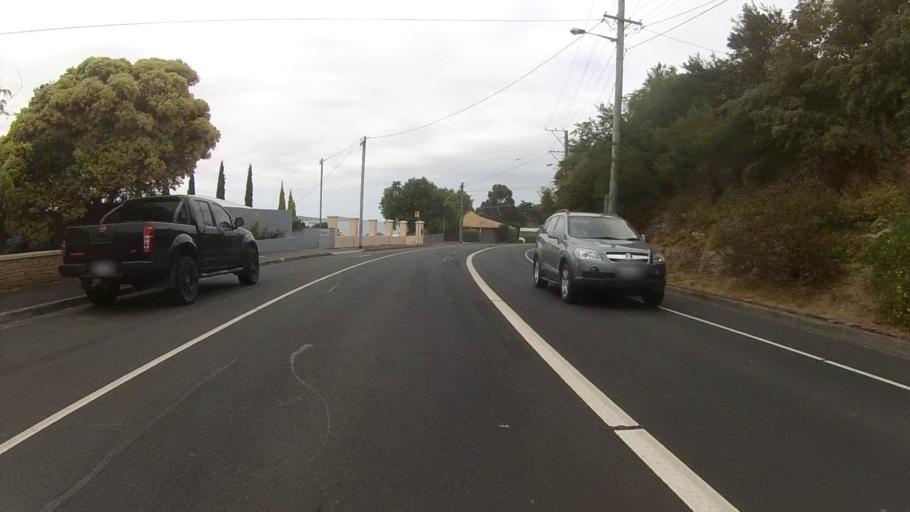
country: AU
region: Tasmania
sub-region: Kingborough
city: Taroona
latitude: -42.9233
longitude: 147.3603
